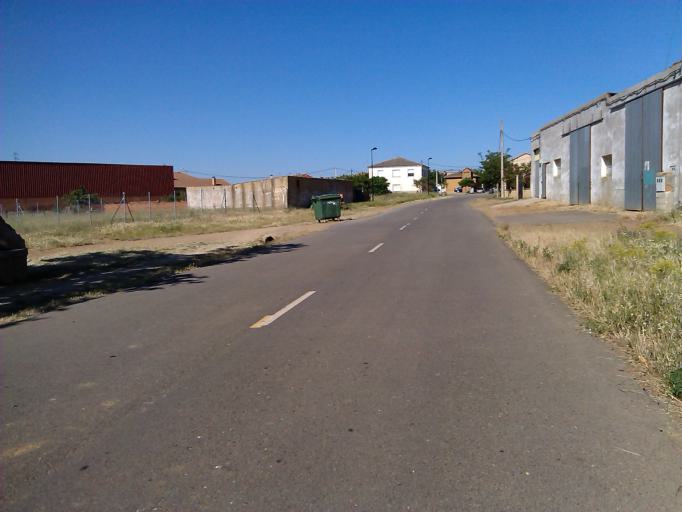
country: ES
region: Castille and Leon
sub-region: Provincia de Leon
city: Bercianos del Real Camino
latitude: 42.3883
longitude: -5.1398
